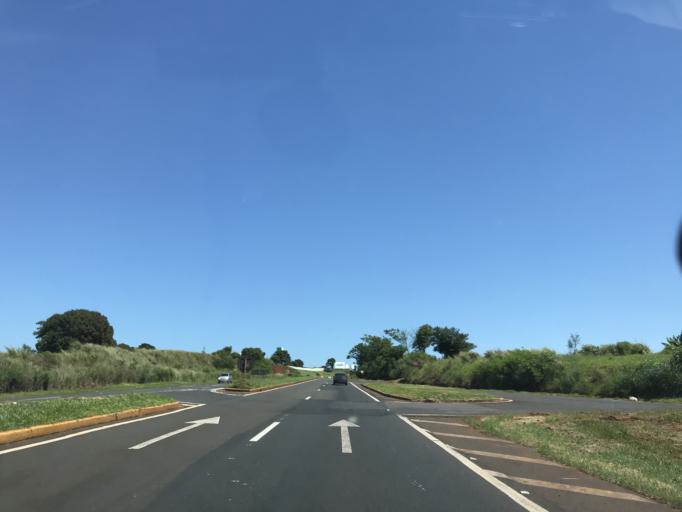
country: BR
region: Parana
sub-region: Marialva
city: Marialva
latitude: -23.4856
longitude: -51.8200
